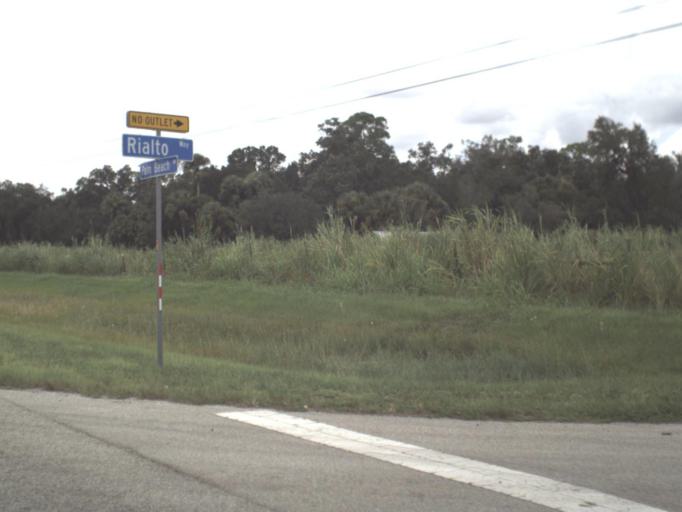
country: US
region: Florida
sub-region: Lee County
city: Olga
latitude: 26.7139
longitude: -81.6624
